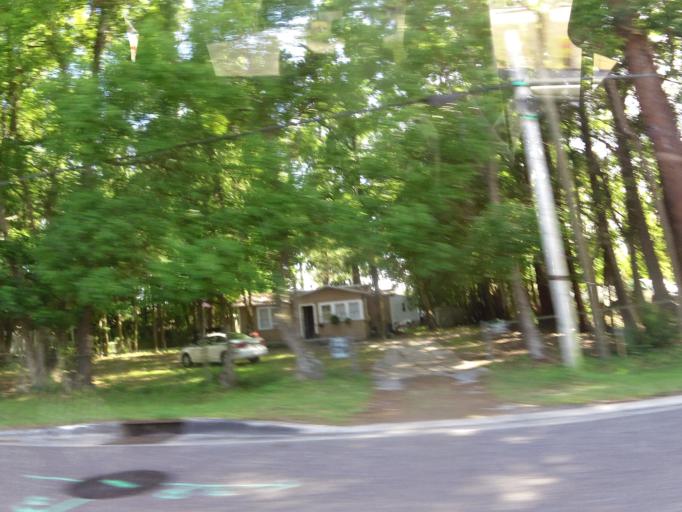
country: US
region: Florida
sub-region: Nassau County
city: Callahan
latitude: 30.5587
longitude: -81.8294
